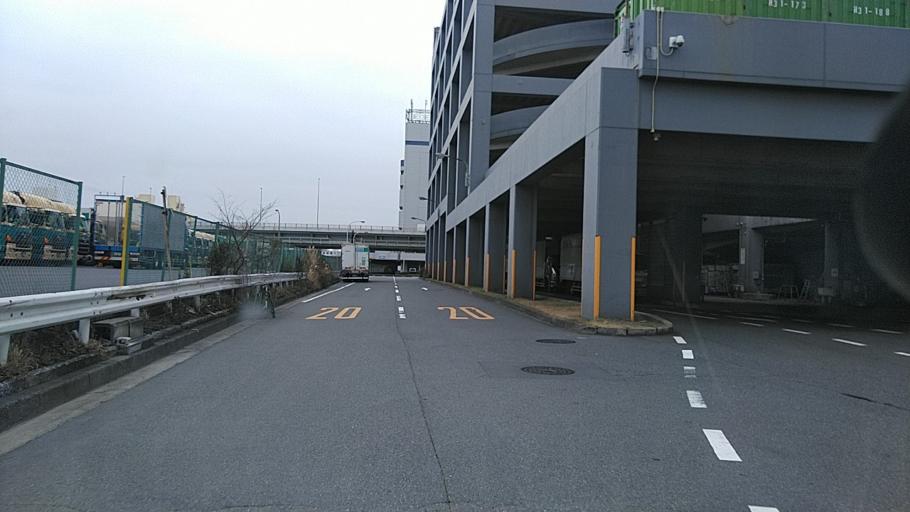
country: JP
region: Kanagawa
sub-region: Kawasaki-shi
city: Kawasaki
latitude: 35.5964
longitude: 139.7613
